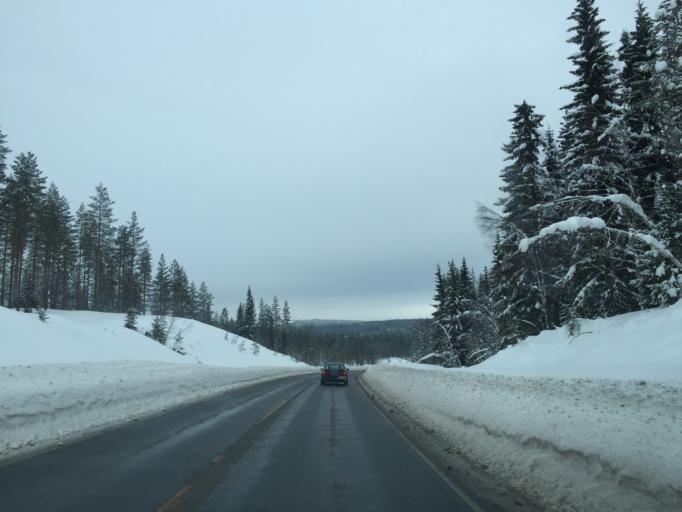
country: NO
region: Hedmark
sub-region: Trysil
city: Innbygda
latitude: 61.0837
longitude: 11.9823
